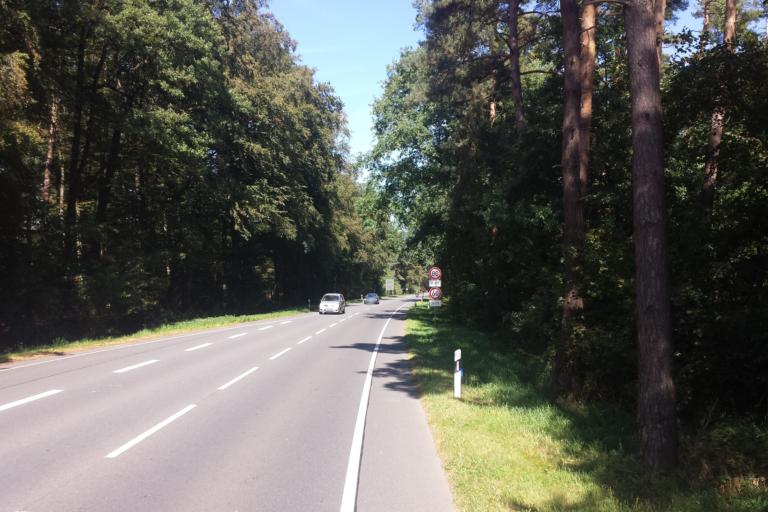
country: DE
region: Hesse
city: Viernheim
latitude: 49.5589
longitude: 8.5834
